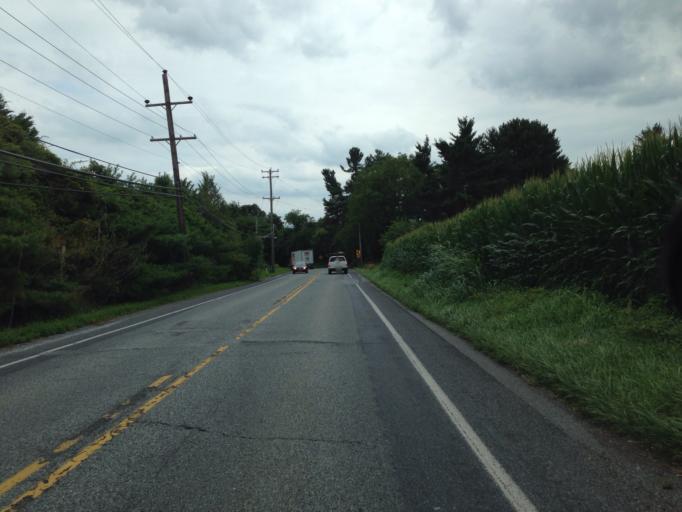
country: US
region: Pennsylvania
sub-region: Chester County
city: West Grove
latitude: 39.7657
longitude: -75.8514
